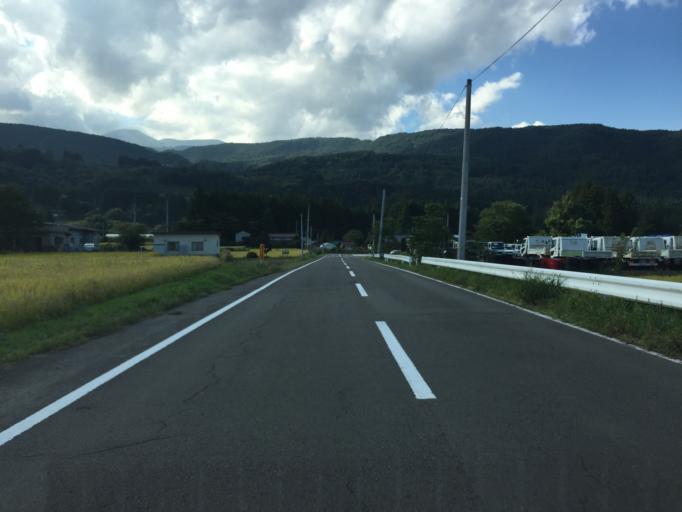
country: JP
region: Fukushima
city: Fukushima-shi
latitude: 37.7113
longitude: 140.3533
